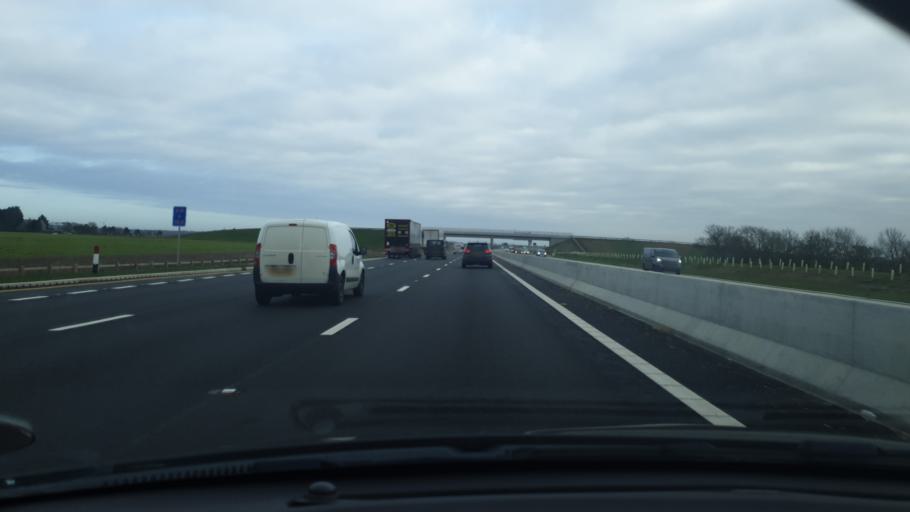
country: GB
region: England
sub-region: Cambridgeshire
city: Hemingford Grey
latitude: 52.2928
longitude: -0.1246
